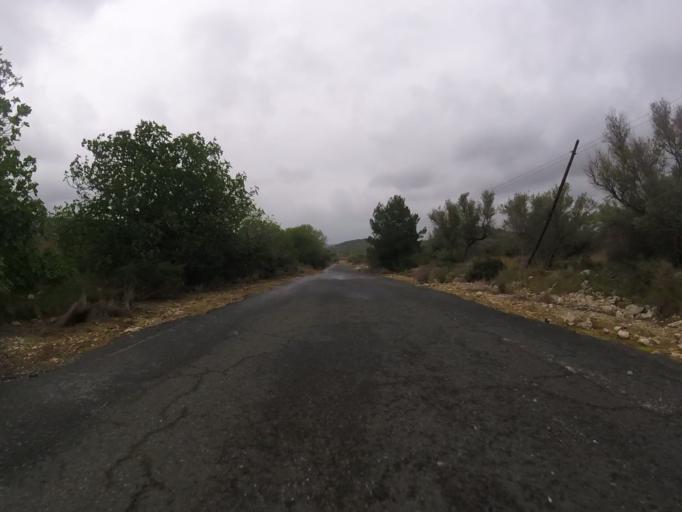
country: ES
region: Valencia
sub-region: Provincia de Castello
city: Alcala de Xivert
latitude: 40.2787
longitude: 0.2269
